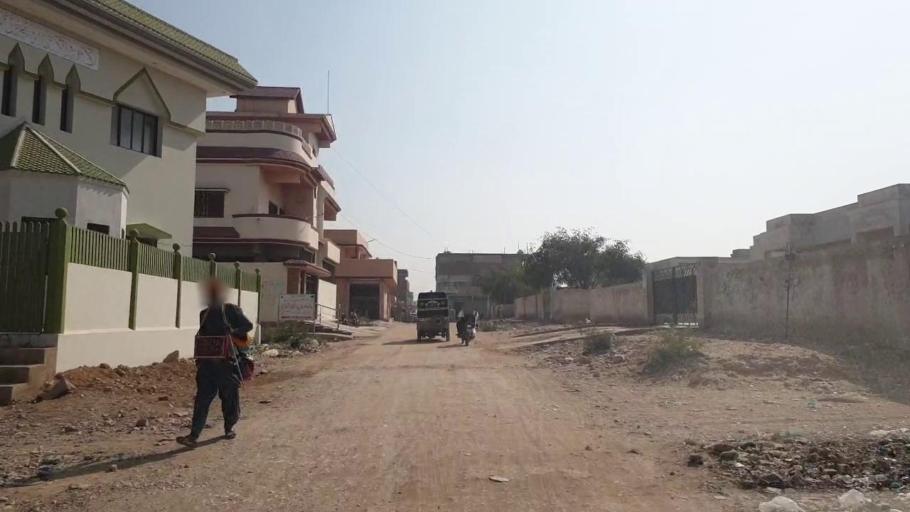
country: PK
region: Sindh
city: Kotri
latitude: 25.3456
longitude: 68.2812
